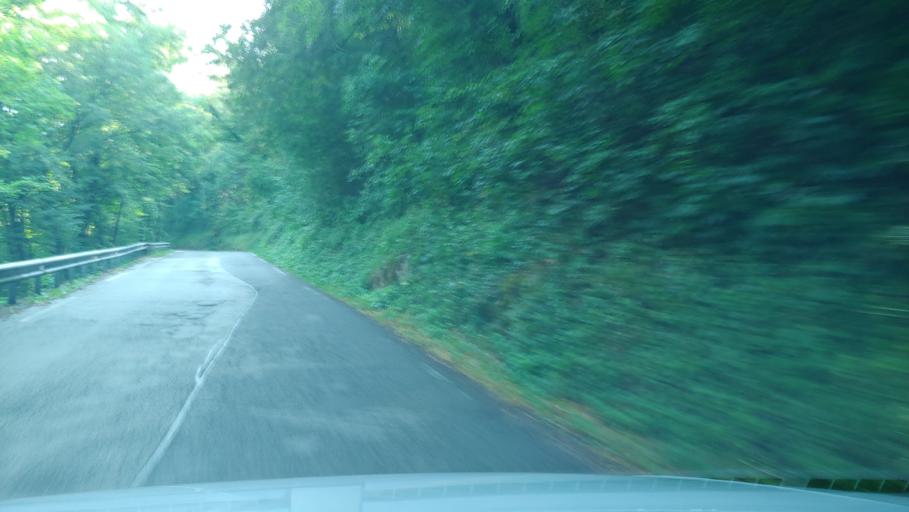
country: SI
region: Komen
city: Komen
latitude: 45.8478
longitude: 13.7899
